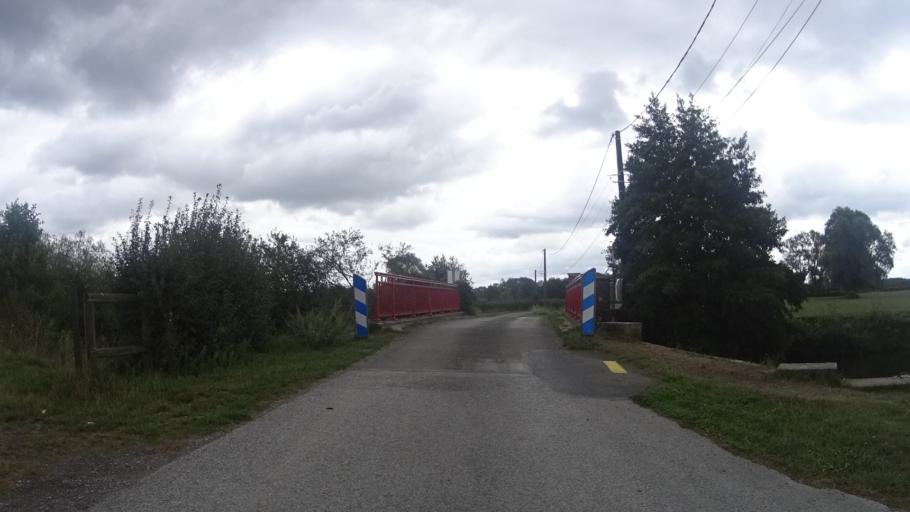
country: FR
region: Nord-Pas-de-Calais
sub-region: Departement du Nord
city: Maroilles
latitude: 50.1428
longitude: 3.7377
